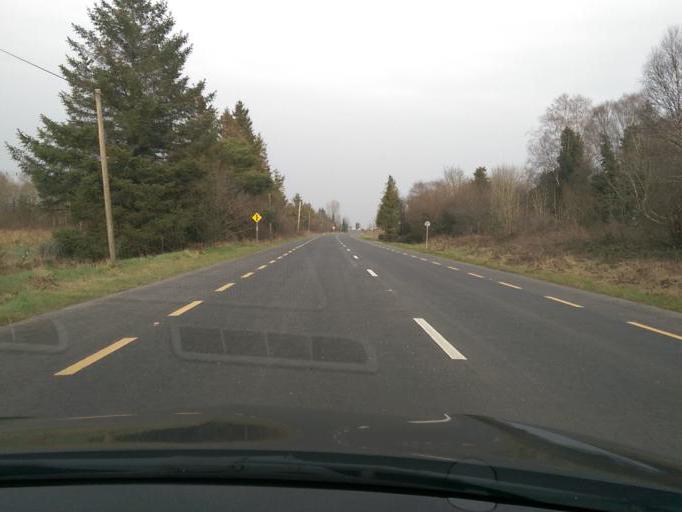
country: IE
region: Connaught
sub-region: Roscommon
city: Roscommon
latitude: 53.6571
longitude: -8.0935
